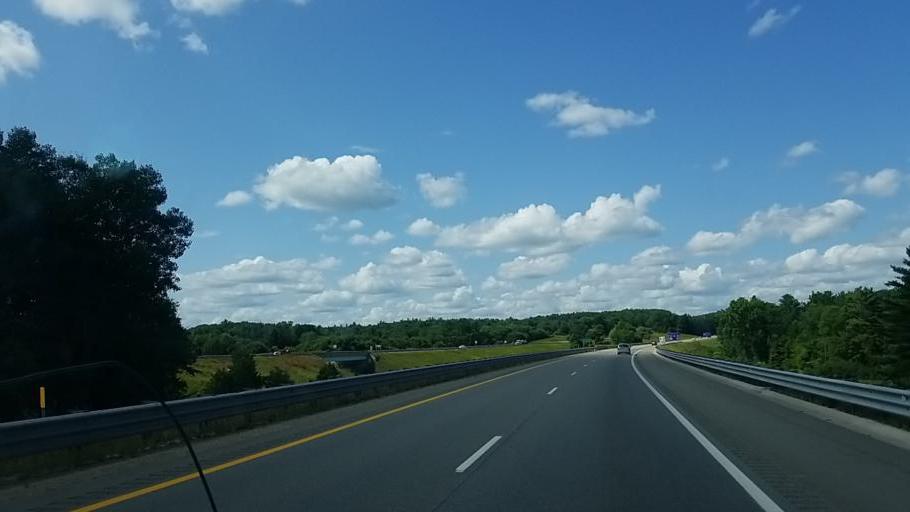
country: US
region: Michigan
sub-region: Mecosta County
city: Big Rapids
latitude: 43.6552
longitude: -85.5190
